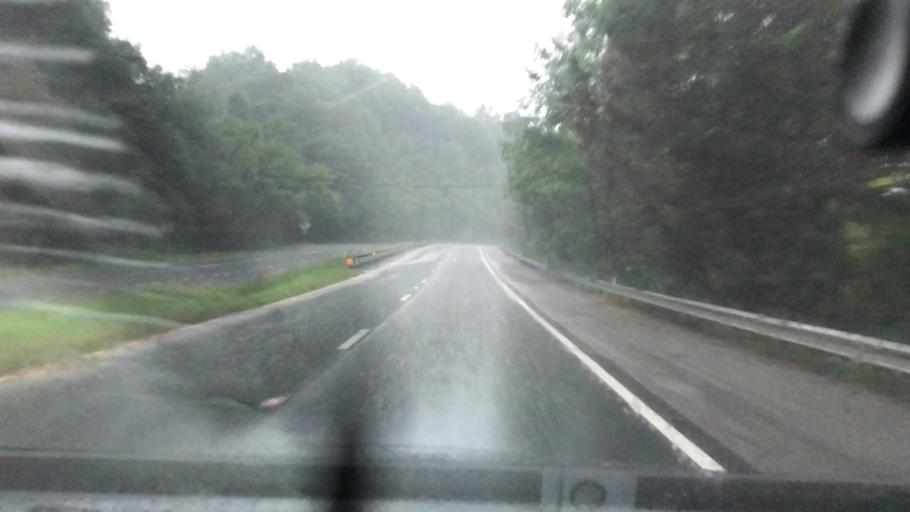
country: US
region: Virginia
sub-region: Giles County
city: Pearisburg
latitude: 37.3477
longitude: -80.7610
